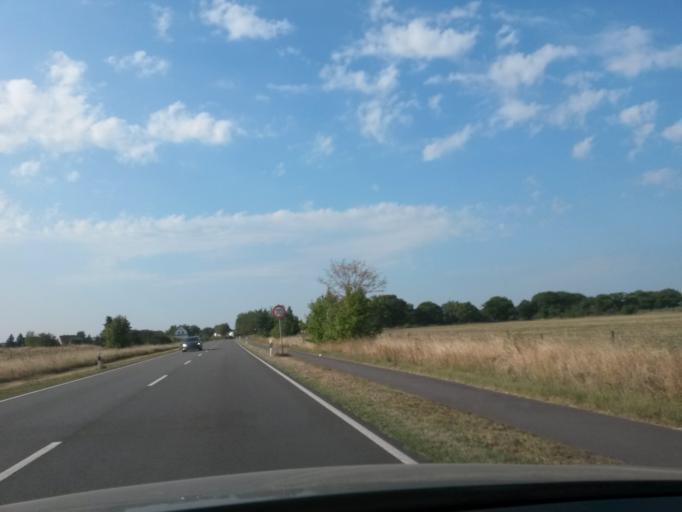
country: DE
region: Saxony-Anhalt
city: Schonhausen
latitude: 52.5464
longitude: 12.0209
